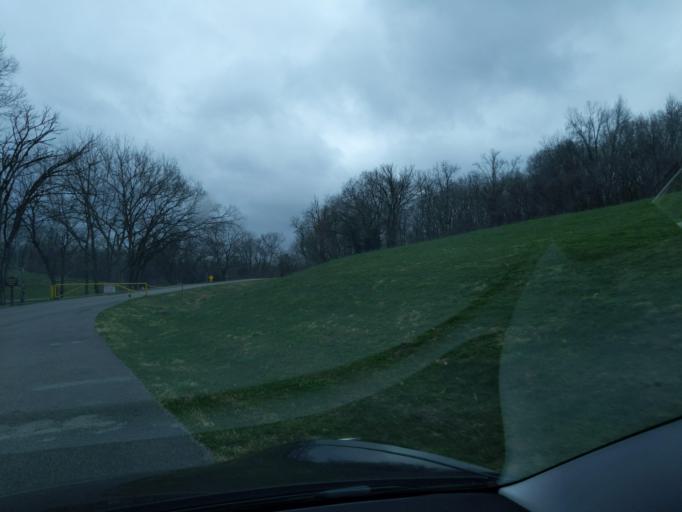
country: US
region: Kentucky
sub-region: Clark County
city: Winchester
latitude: 37.8953
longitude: -84.2670
